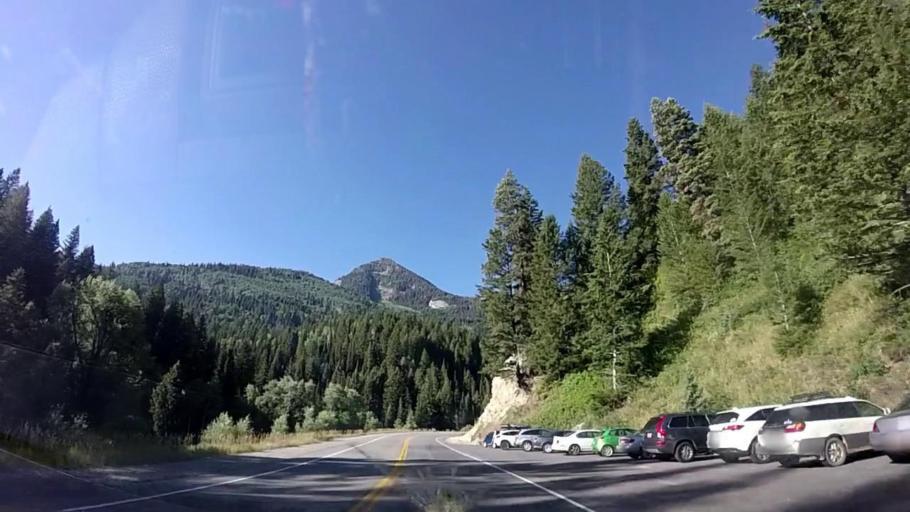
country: US
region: Utah
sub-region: Summit County
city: Summit Park
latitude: 40.6492
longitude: -111.6616
